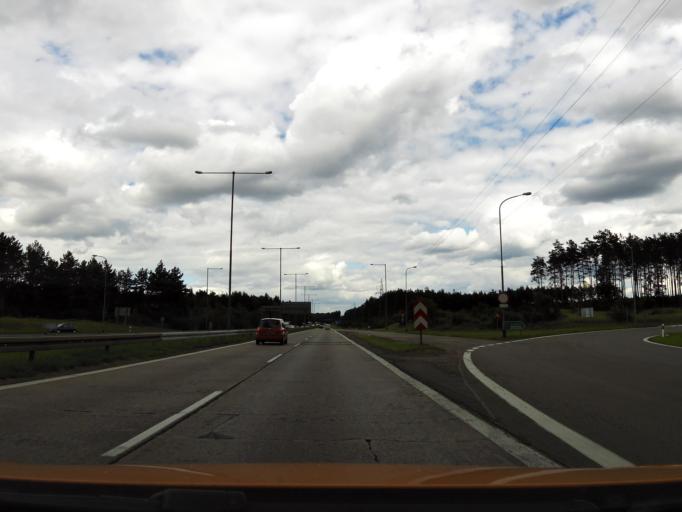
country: PL
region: West Pomeranian Voivodeship
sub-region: Powiat gryfinski
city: Stare Czarnowo
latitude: 53.3750
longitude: 14.7029
